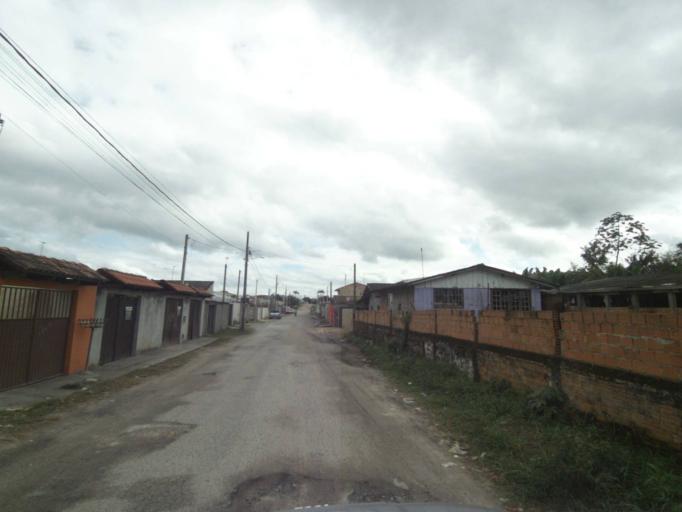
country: BR
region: Parana
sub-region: Paranagua
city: Paranagua
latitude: -25.5718
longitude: -48.5646
